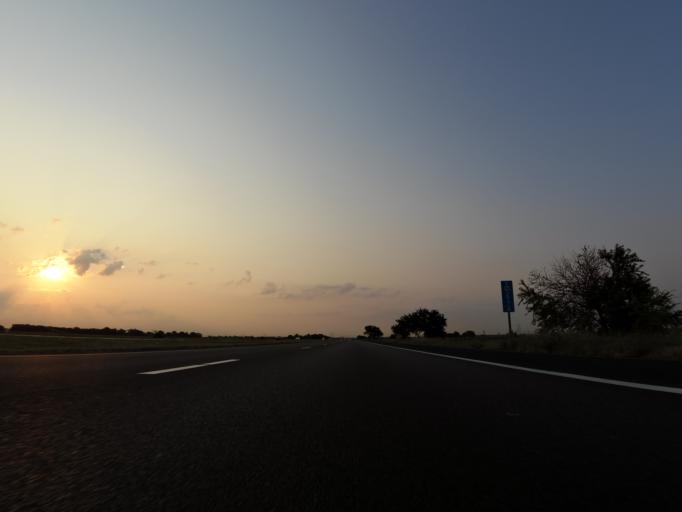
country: US
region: Kansas
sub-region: Sedgwick County
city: Maize
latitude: 37.8019
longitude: -97.4929
